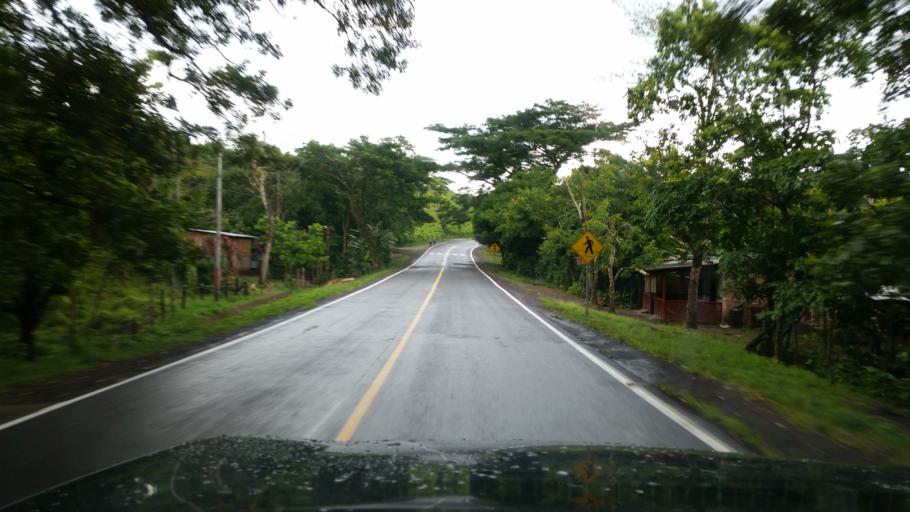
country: NI
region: Matagalpa
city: San Ramon
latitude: 13.0507
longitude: -85.7621
